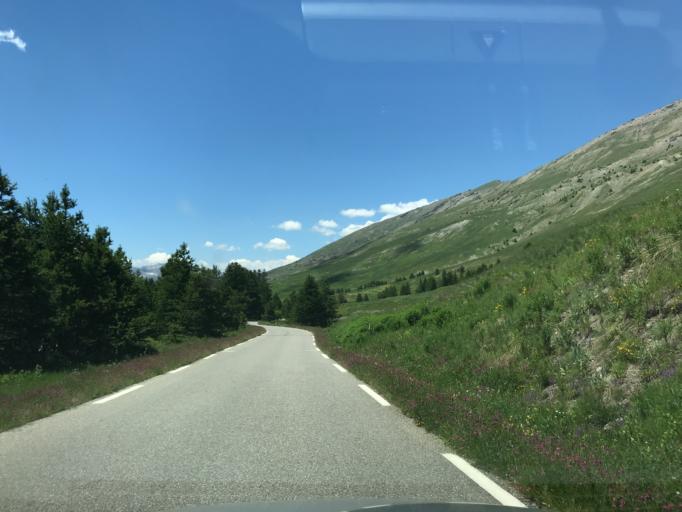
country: IT
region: Piedmont
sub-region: Provincia di Cuneo
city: Pontechianale
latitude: 44.7161
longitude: 6.9137
